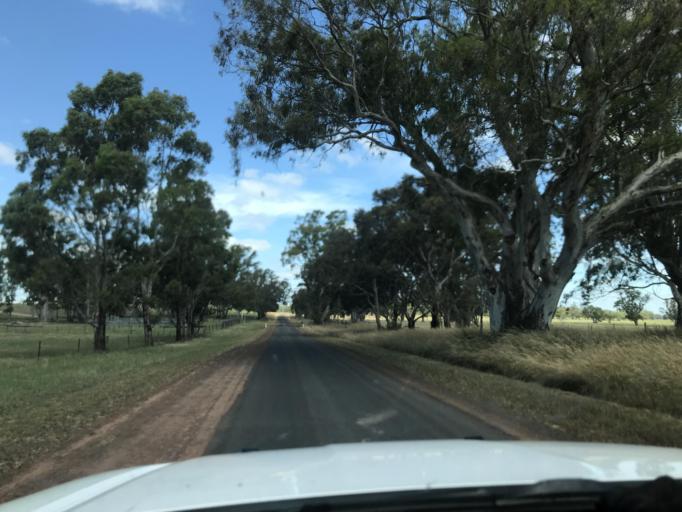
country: AU
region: South Australia
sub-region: Naracoorte and Lucindale
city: Naracoorte
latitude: -36.8630
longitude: 141.1689
